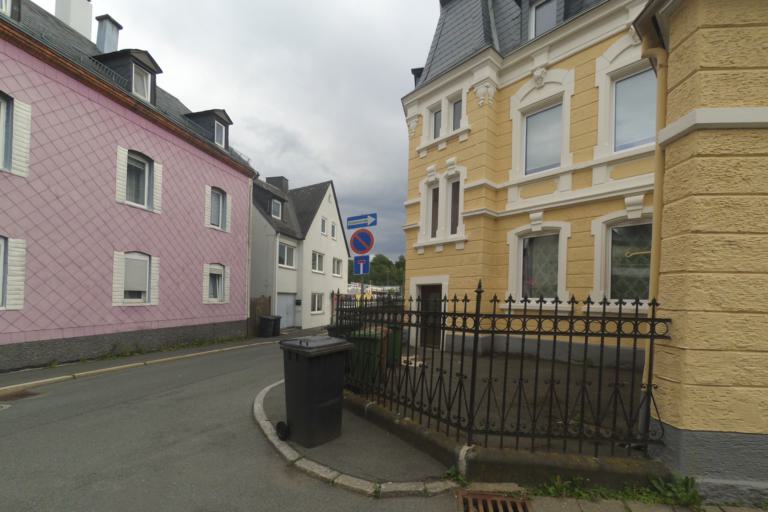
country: DE
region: Bavaria
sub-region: Upper Franconia
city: Munchberg
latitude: 50.1920
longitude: 11.7835
